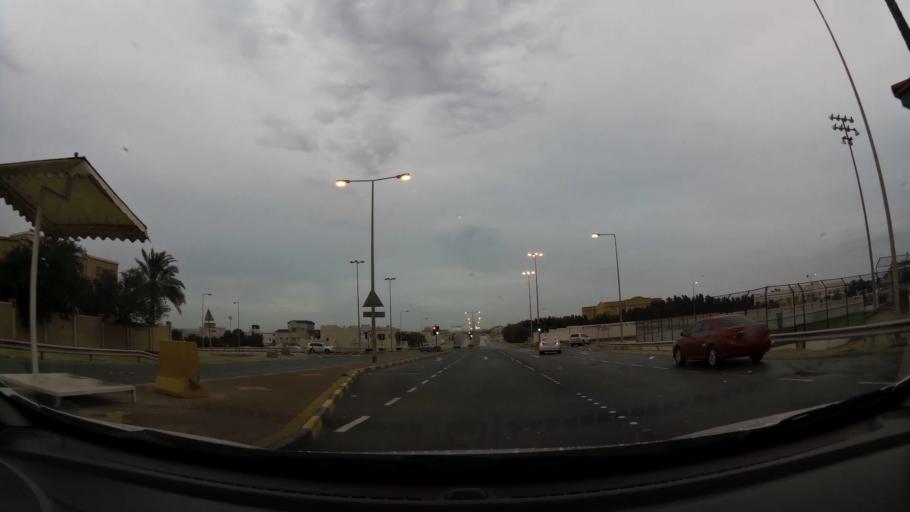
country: BH
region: Central Governorate
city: Madinat Hamad
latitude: 26.1405
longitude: 50.5171
